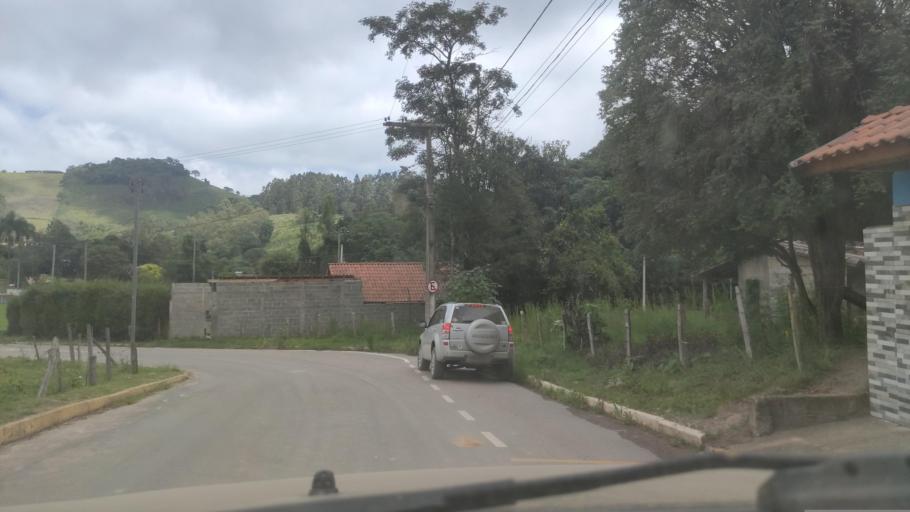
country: BR
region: Minas Gerais
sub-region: Cambui
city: Cambui
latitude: -22.6592
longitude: -45.9156
